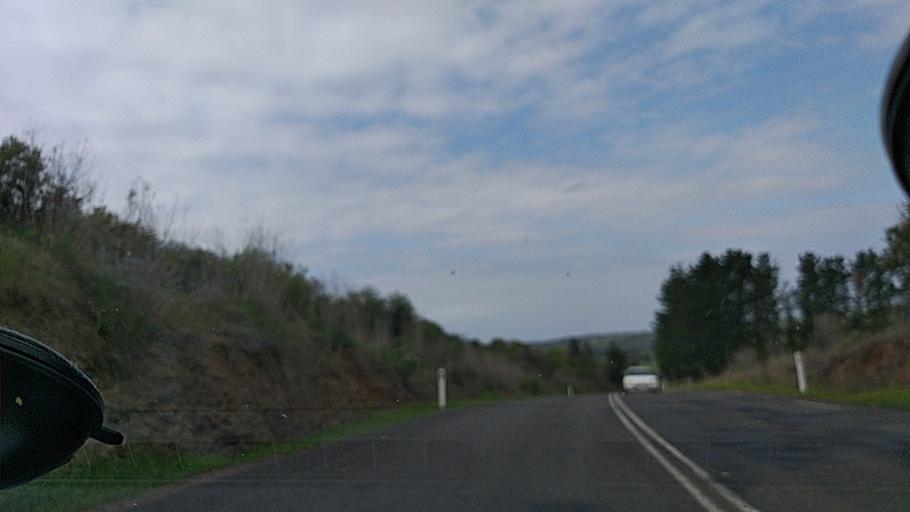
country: AU
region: New South Wales
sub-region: Camden
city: Camden South
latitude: -34.1280
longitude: 150.7166
